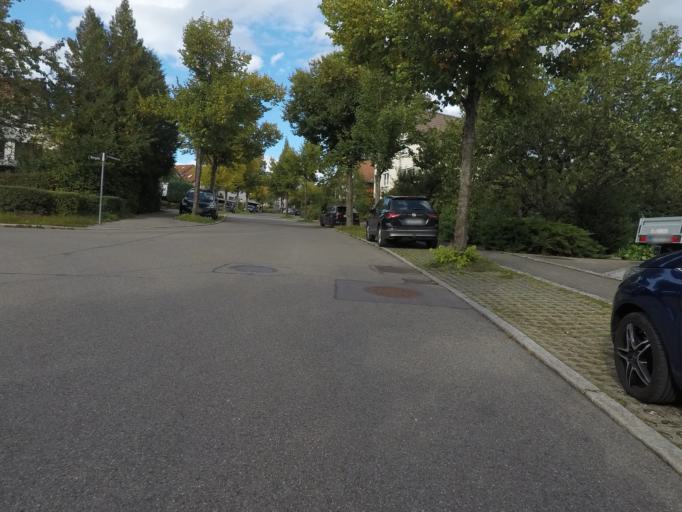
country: DE
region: Baden-Wuerttemberg
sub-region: Tuebingen Region
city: Pfullingen
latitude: 48.4605
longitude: 9.2341
